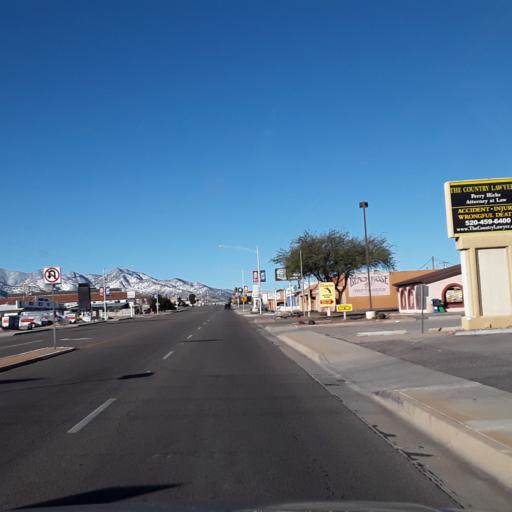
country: US
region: Arizona
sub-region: Cochise County
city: Sierra Vista
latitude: 31.5547
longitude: -110.2914
